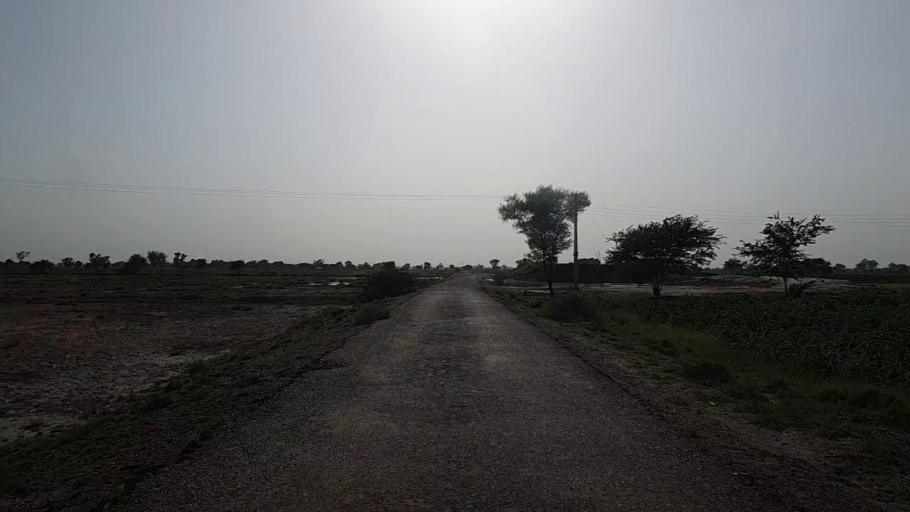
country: PK
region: Sindh
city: Pad Idan
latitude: 26.8531
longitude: 68.3117
